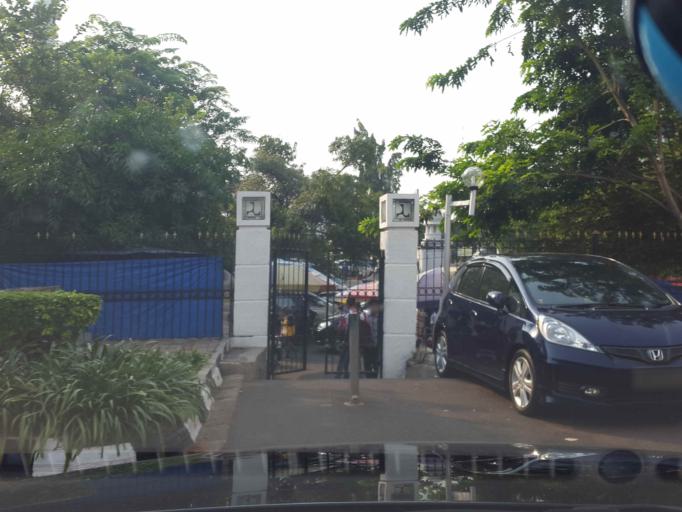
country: ID
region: Jakarta Raya
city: Jakarta
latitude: -6.2354
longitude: 106.8005
